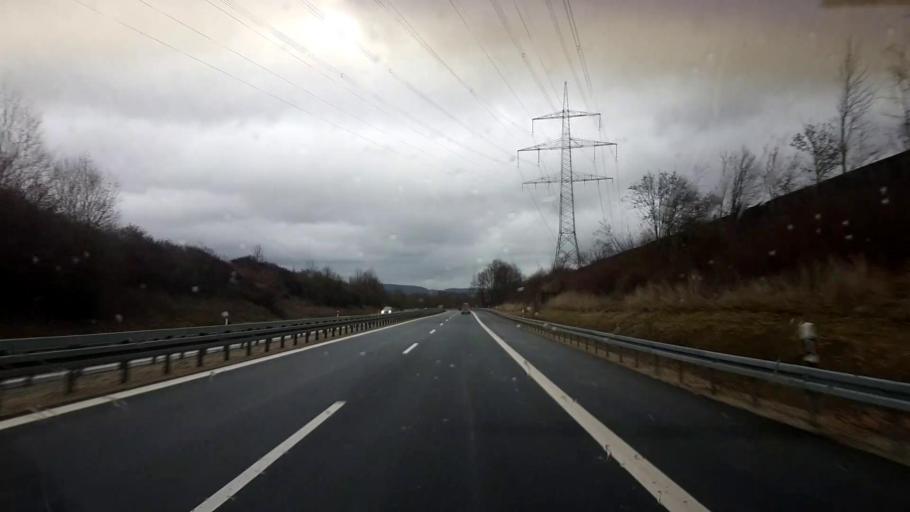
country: DE
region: Bavaria
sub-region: Upper Franconia
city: Schesslitz
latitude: 49.9672
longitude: 10.9983
